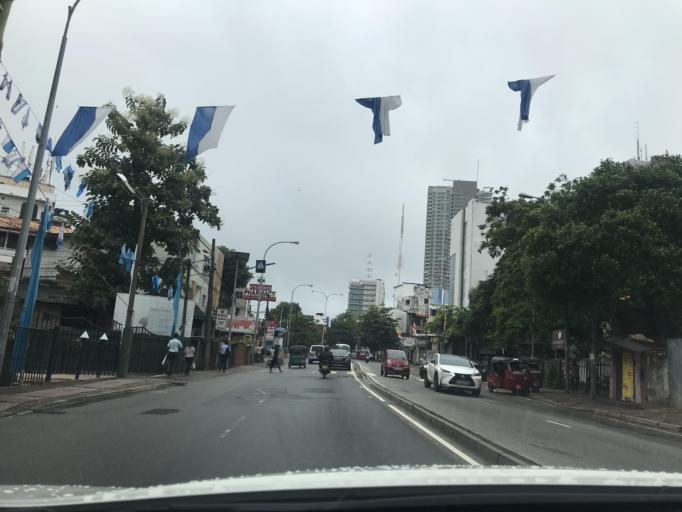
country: LK
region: Western
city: Colombo
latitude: 6.9225
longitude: 79.8647
